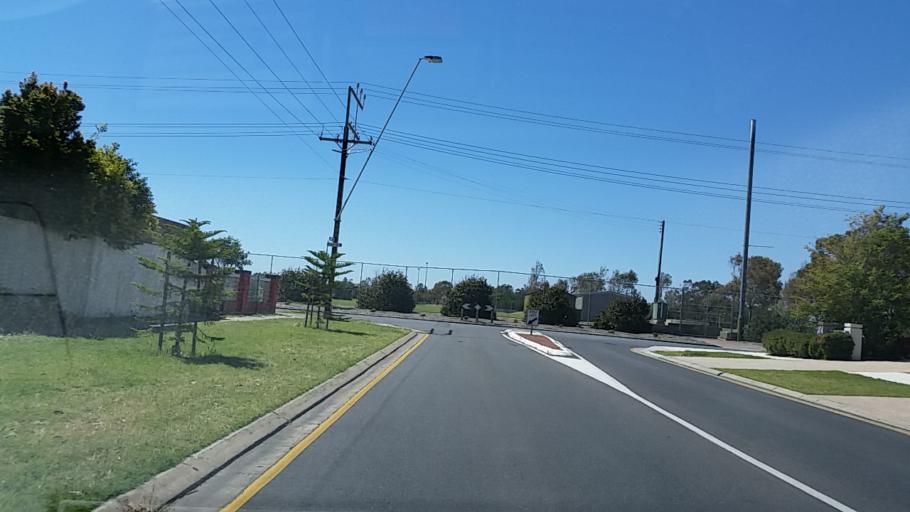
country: AU
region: South Australia
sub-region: Charles Sturt
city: Grange
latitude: -34.8977
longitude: 138.4921
